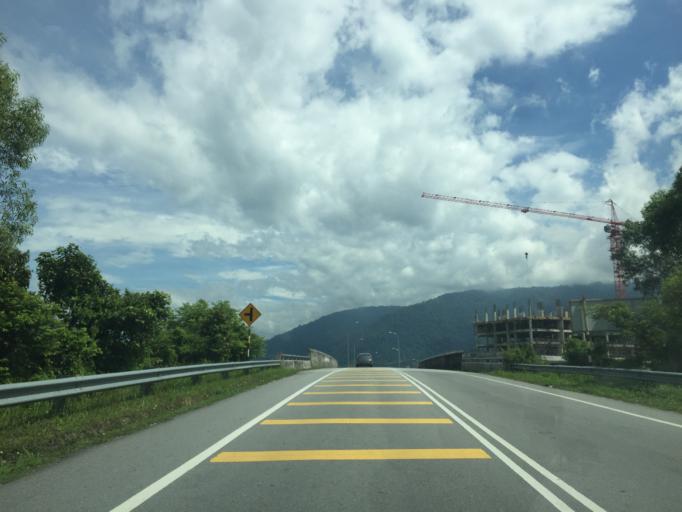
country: MY
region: Perak
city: Kampar
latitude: 4.3269
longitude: 101.1306
